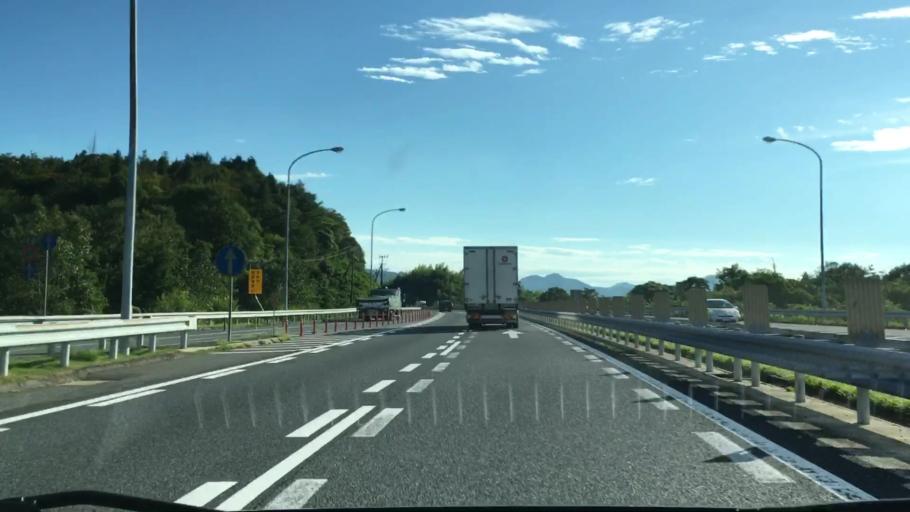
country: JP
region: Yamaguchi
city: Yanai
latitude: 34.0986
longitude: 132.1004
